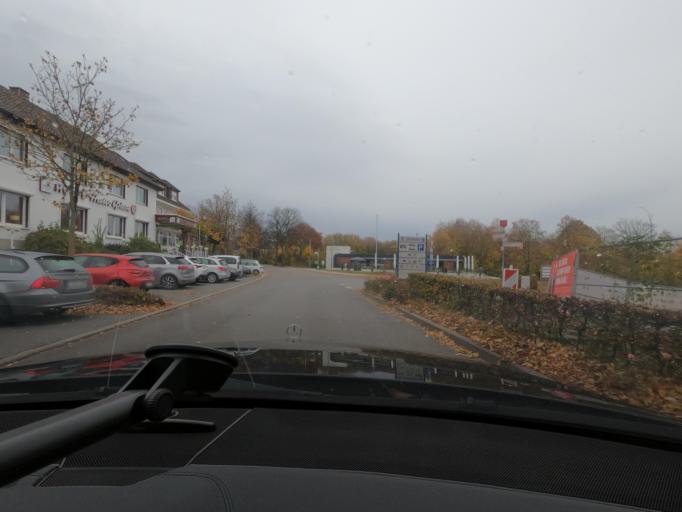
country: DE
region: North Rhine-Westphalia
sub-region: Regierungsbezirk Arnsberg
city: Mohnesee
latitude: 51.4933
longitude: 8.1251
